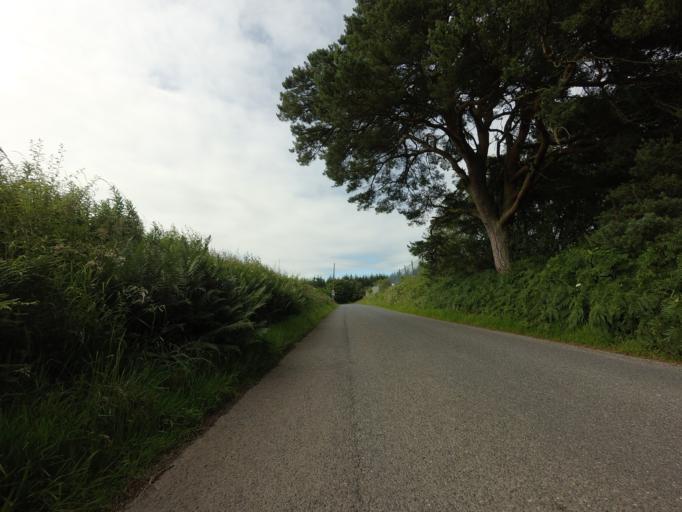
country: GB
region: Scotland
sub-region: Aberdeenshire
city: Turriff
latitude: 57.5350
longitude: -2.4027
